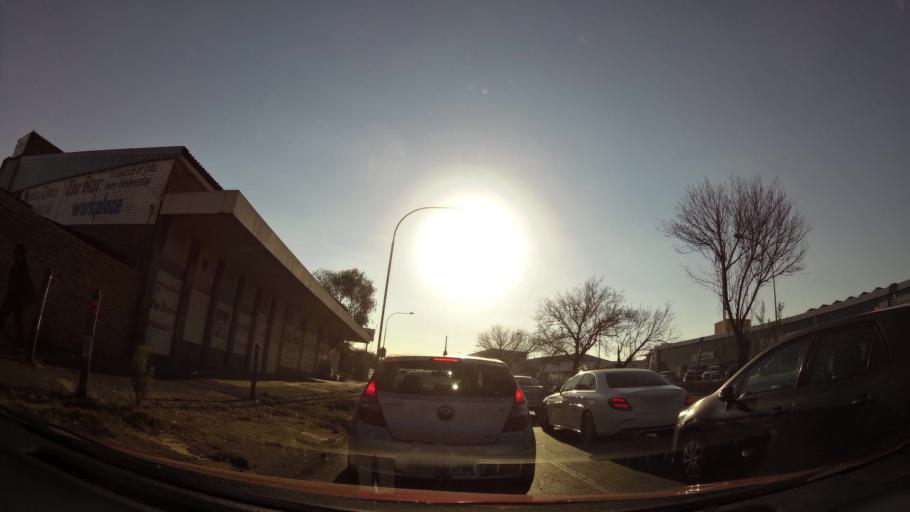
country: ZA
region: Gauteng
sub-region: City of Johannesburg Metropolitan Municipality
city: Johannesburg
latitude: -26.2310
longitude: 28.0275
